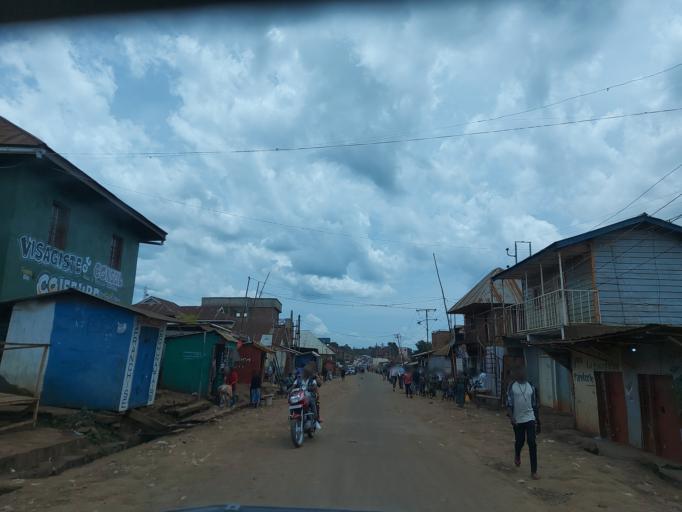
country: CD
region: South Kivu
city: Bukavu
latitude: -2.2988
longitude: 28.7981
